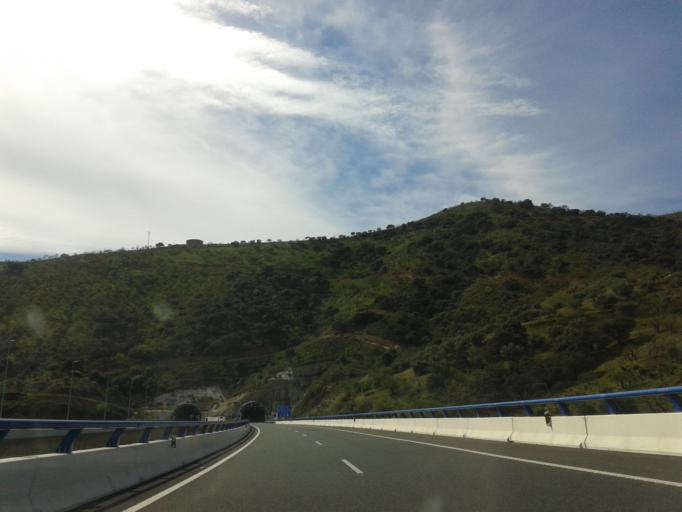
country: ES
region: Andalusia
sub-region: Provincia de Malaga
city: Casabermeja
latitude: 36.8731
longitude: -4.4831
